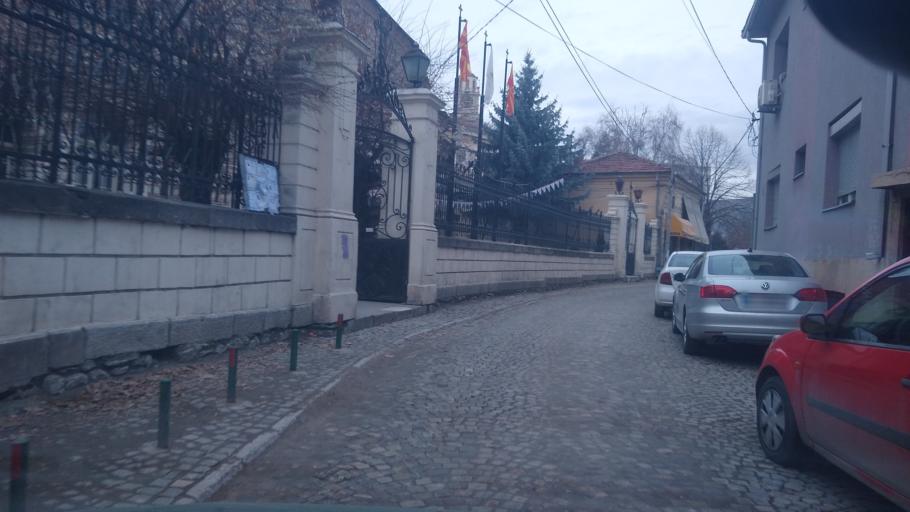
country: MK
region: Bitola
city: Bitola
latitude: 41.0297
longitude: 21.3343
